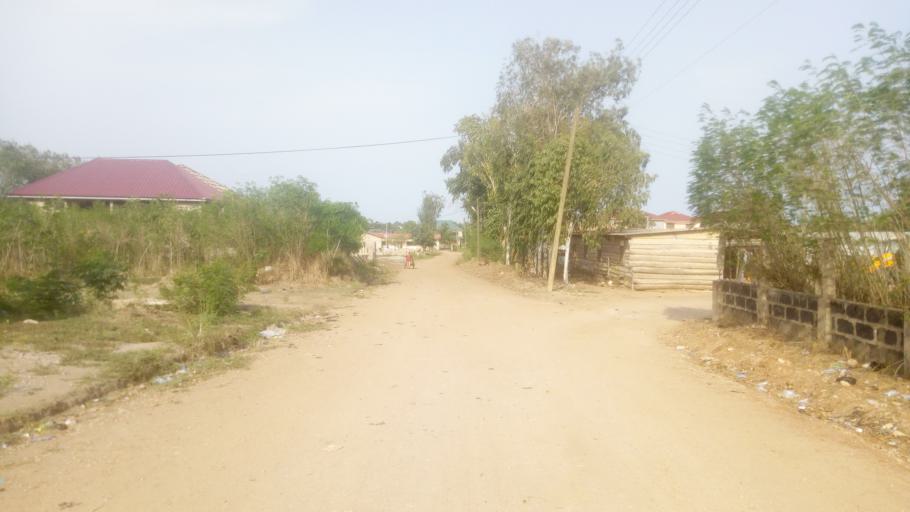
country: GH
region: Central
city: Winneba
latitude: 5.3784
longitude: -0.6400
